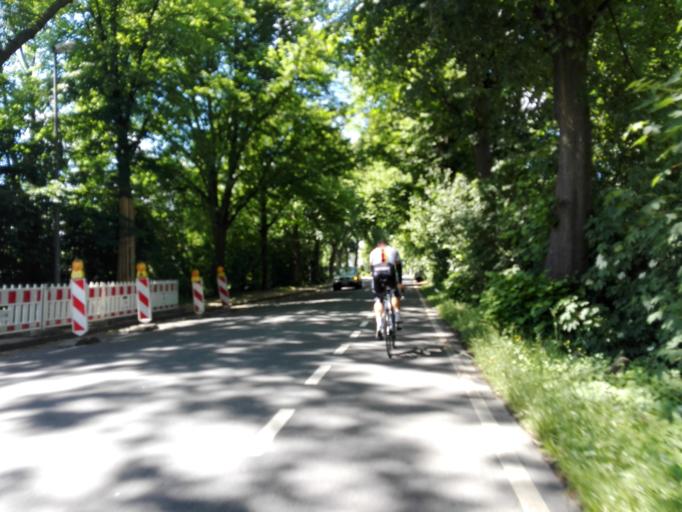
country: DE
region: North Rhine-Westphalia
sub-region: Regierungsbezirk Arnsberg
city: Unna
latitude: 51.5356
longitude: 7.7058
